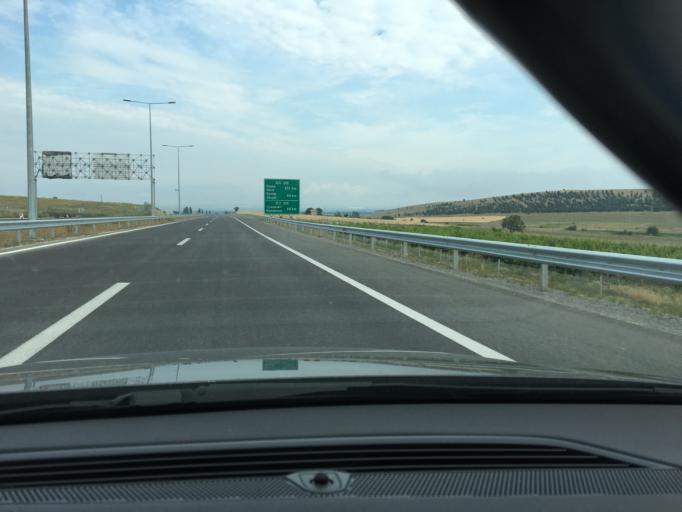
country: MK
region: Stip
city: Shtip
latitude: 41.7854
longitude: 22.1195
